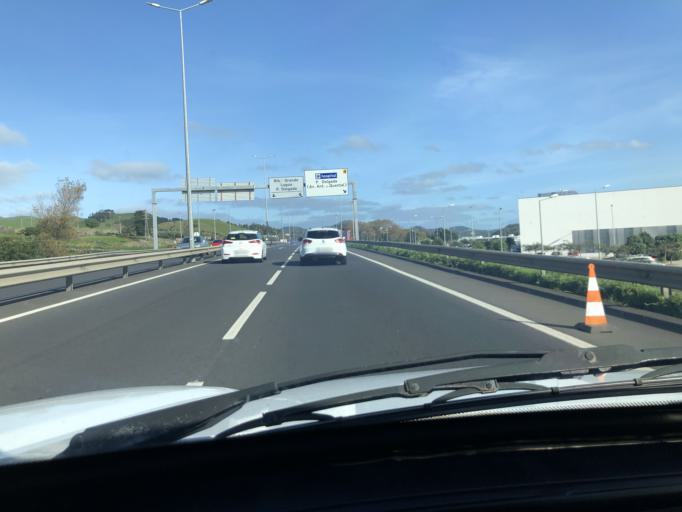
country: PT
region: Azores
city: Ponta Delgada
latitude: 37.7530
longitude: -25.6786
